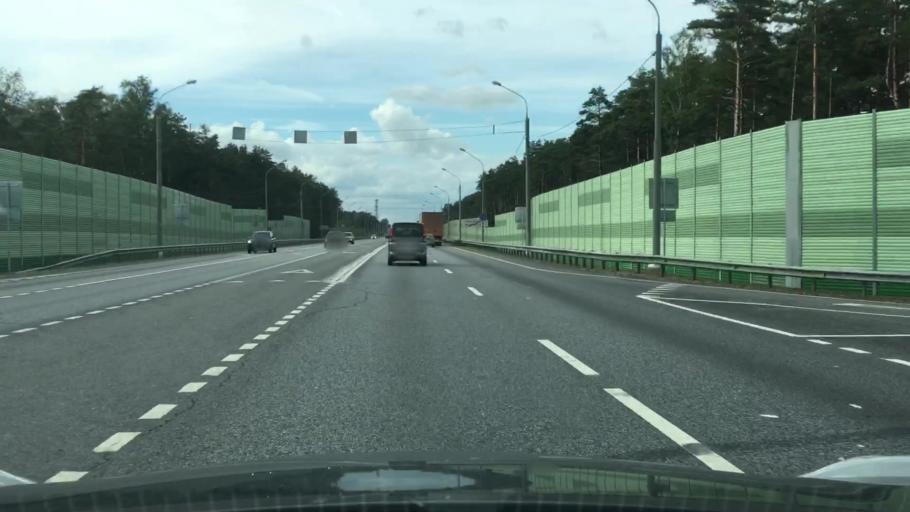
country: RU
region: Tverskaya
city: Radchenko
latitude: 56.6798
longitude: 36.3906
